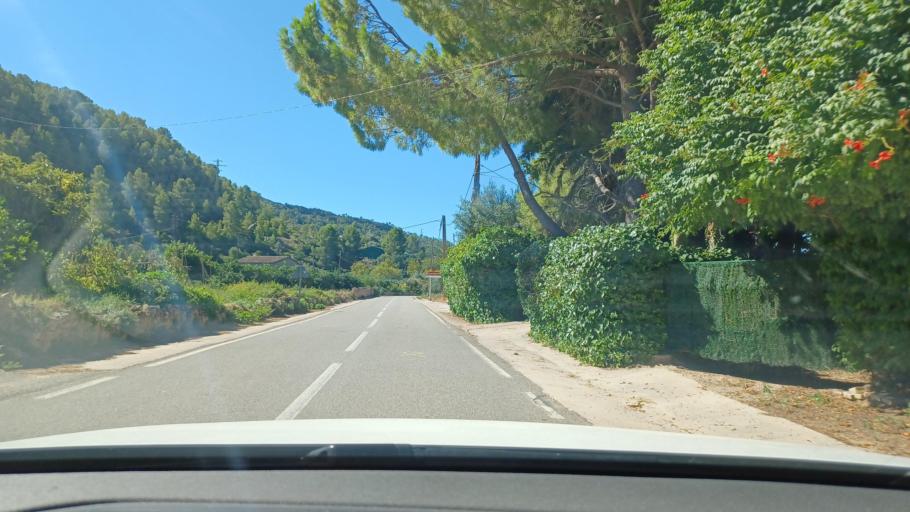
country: ES
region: Catalonia
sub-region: Provincia de Tarragona
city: Benifallet
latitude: 40.9713
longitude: 0.5155
